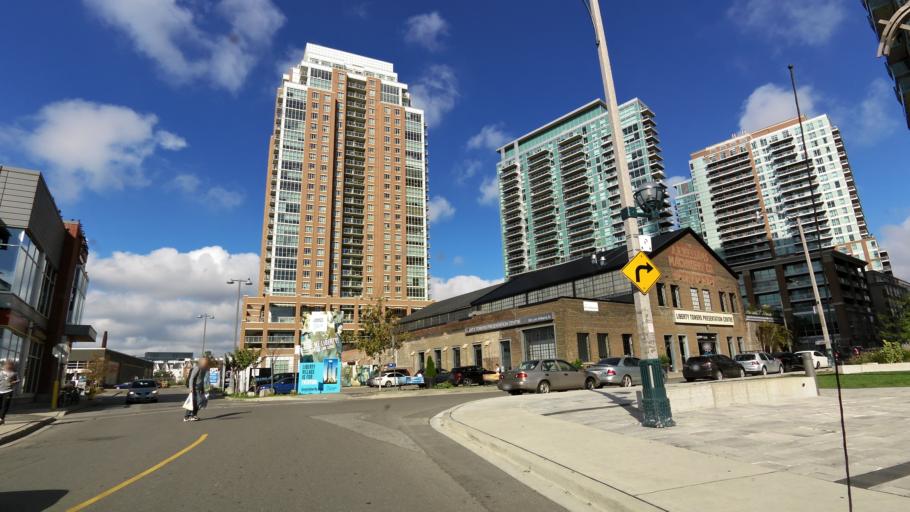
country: CA
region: Ontario
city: Toronto
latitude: 43.6388
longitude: -79.4172
